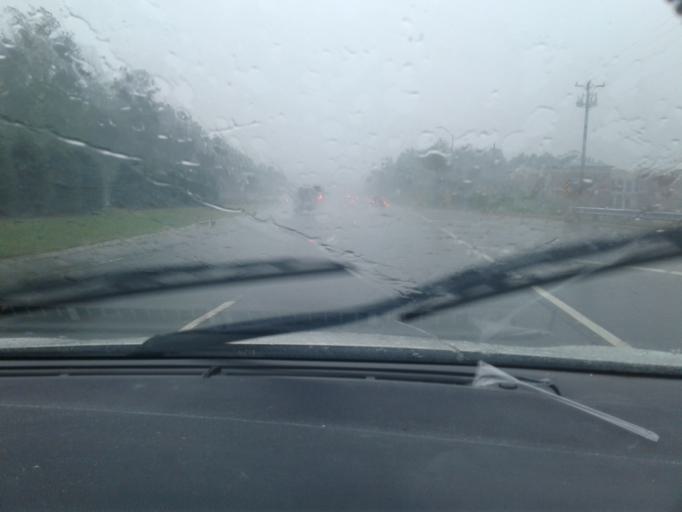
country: US
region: North Carolina
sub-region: Wake County
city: Holly Springs
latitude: 35.6559
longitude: -78.8486
